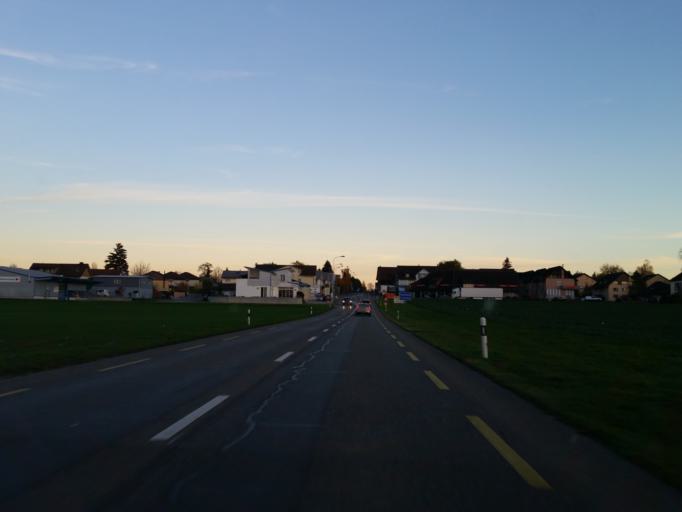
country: CH
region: Thurgau
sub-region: Kreuzlingen District
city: Munsterlingen
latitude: 47.6293
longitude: 9.2429
